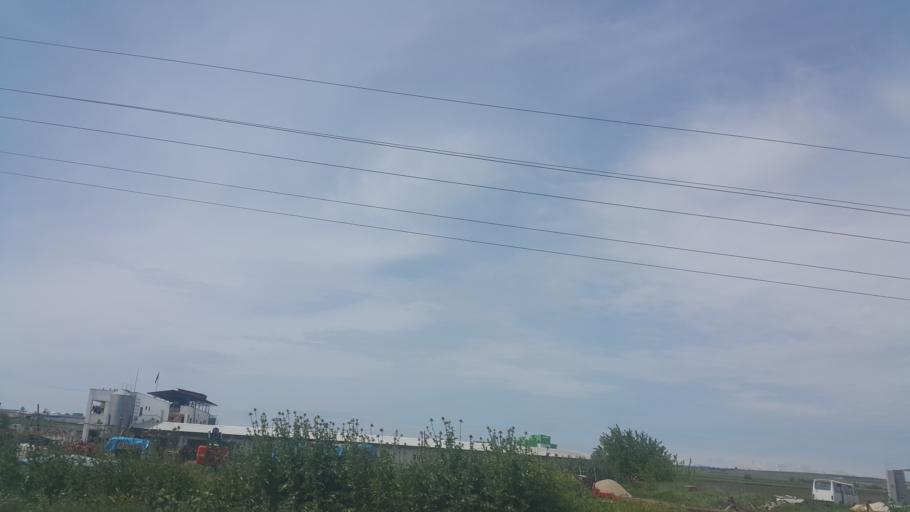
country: TR
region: Adana
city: Yakapinar
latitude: 36.9835
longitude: 35.6601
